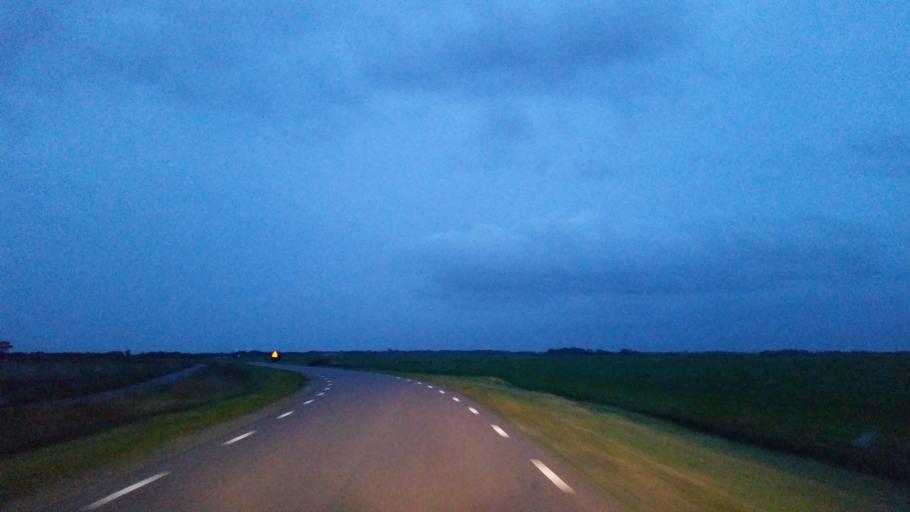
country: NL
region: Friesland
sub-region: Gemeente Leeuwarden
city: Camminghaburen
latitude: 53.2280
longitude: 5.8341
